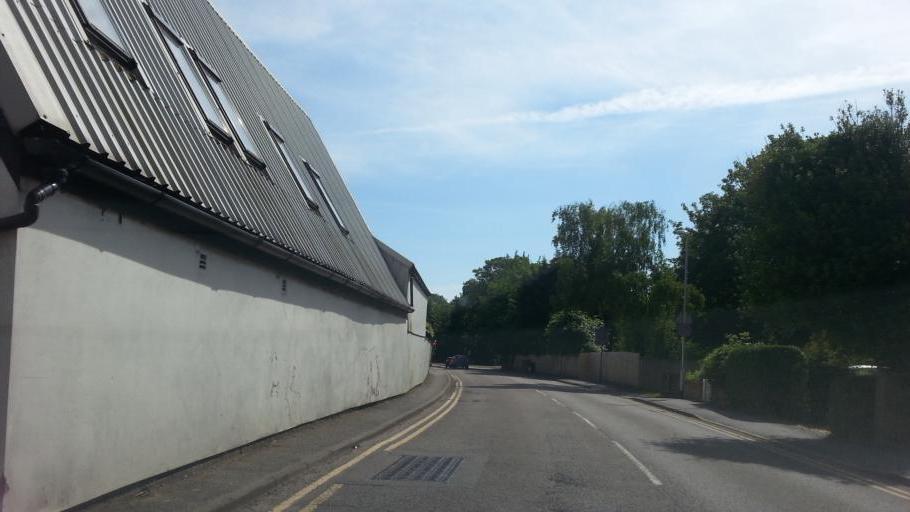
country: GB
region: England
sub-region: Cambridgeshire
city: Sawston
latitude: 52.1482
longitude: 0.1394
